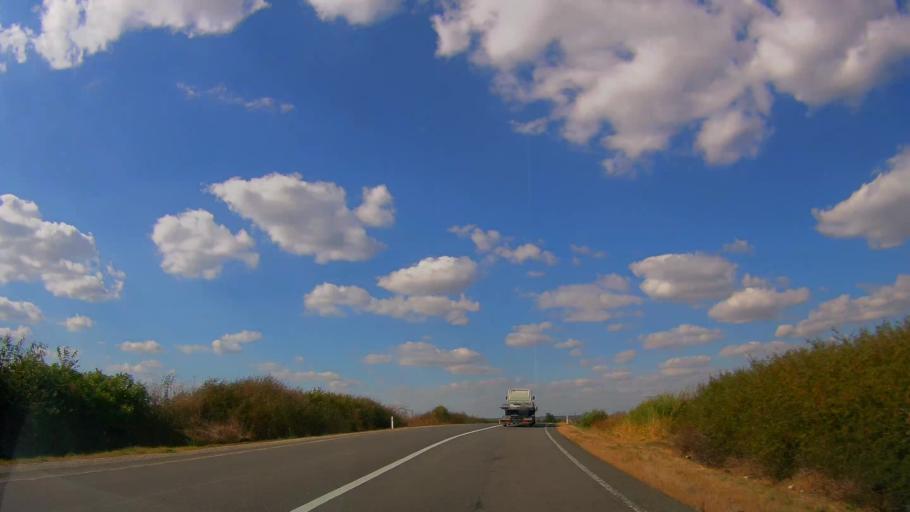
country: RO
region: Salaj
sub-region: Comuna Bobota
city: Dersida
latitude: 47.3615
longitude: 22.7947
